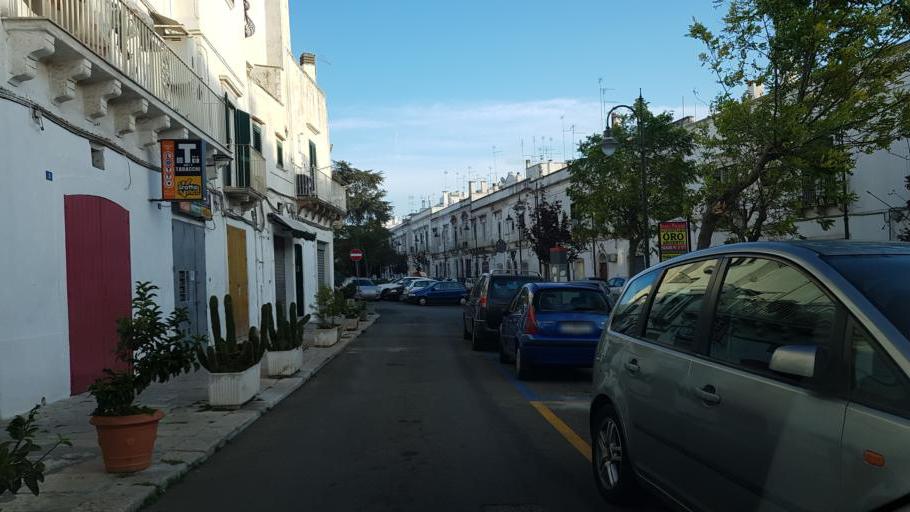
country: IT
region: Apulia
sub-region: Provincia di Taranto
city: Martina Franca
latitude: 40.7043
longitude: 17.3345
